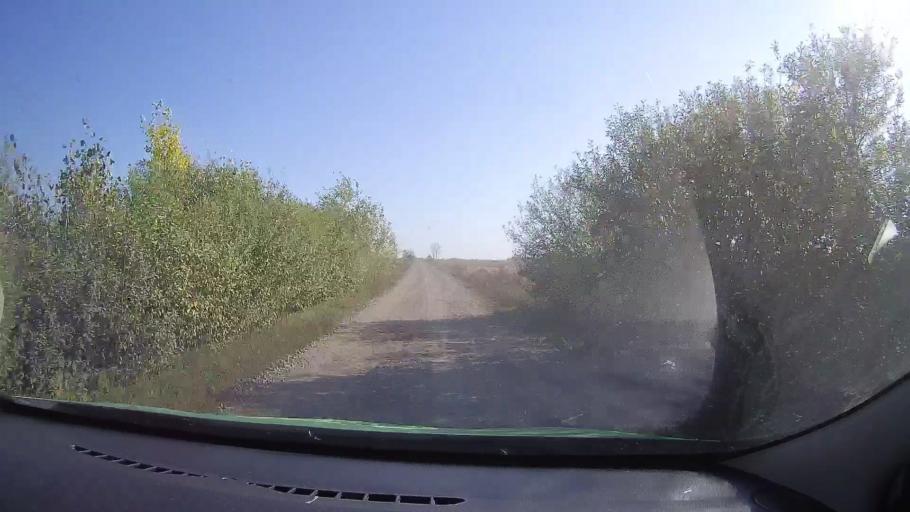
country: RO
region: Satu Mare
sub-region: Comuna Berveni
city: Berveni
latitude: 47.7360
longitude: 22.4428
